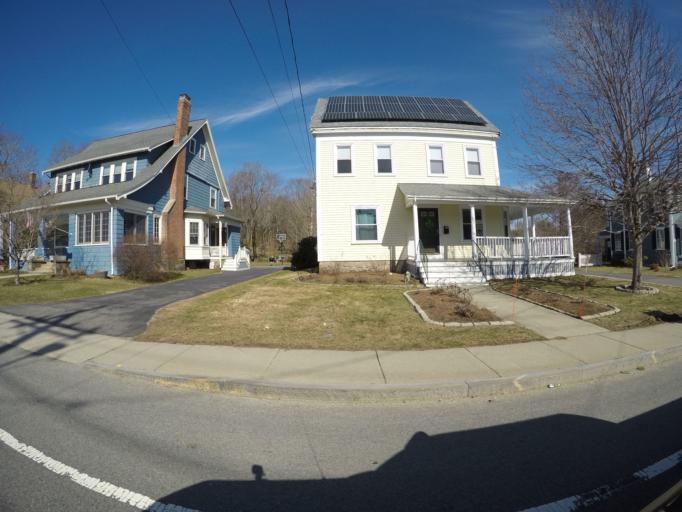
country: US
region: Massachusetts
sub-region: Bristol County
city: Easton
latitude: 42.0660
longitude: -71.0967
